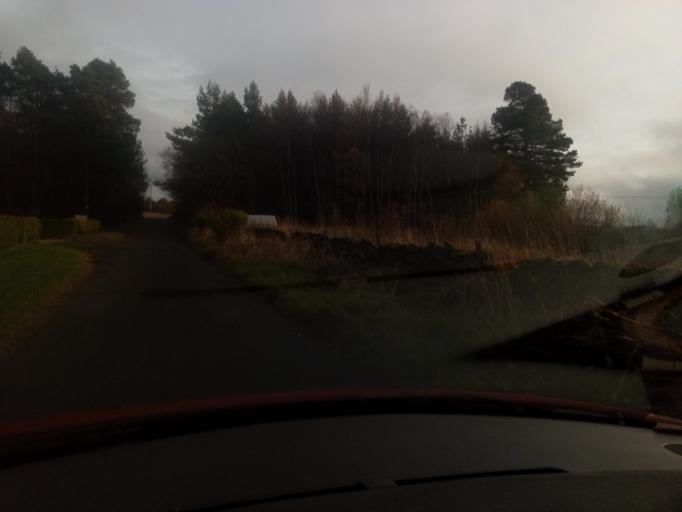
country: GB
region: Scotland
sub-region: The Scottish Borders
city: Jedburgh
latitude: 55.4817
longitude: -2.5758
